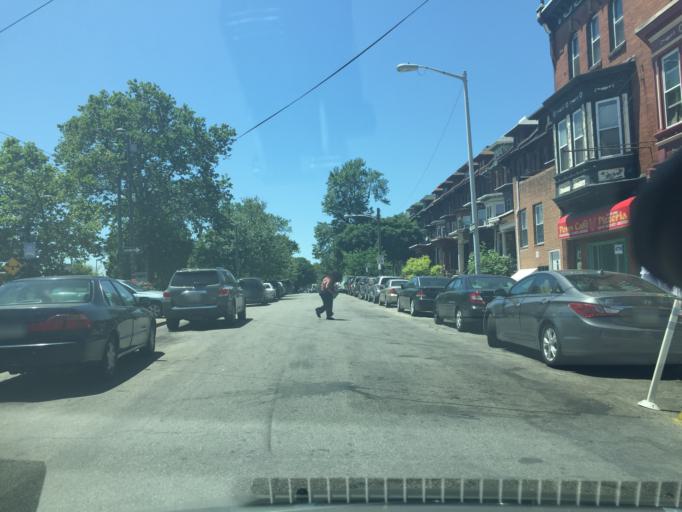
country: US
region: Pennsylvania
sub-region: Delaware County
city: Millbourne
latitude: 39.9482
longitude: -75.2215
